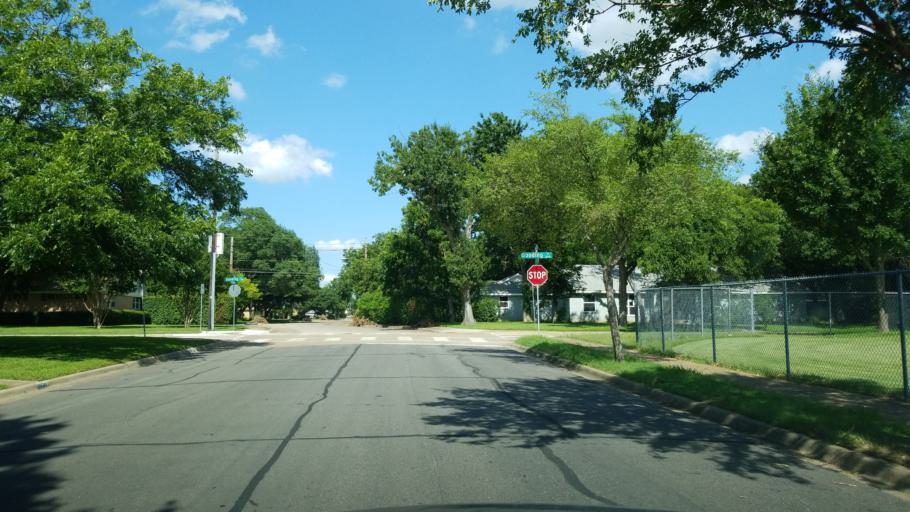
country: US
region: Texas
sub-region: Dallas County
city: University Park
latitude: 32.8835
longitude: -96.8437
